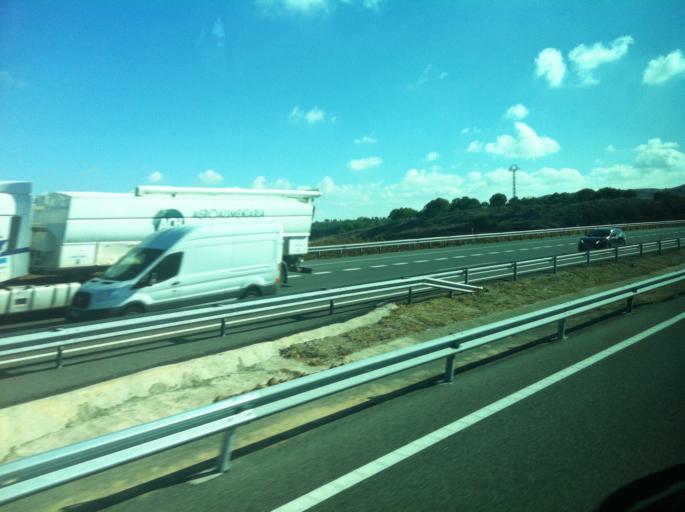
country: ES
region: Castille and Leon
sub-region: Provincia de Burgos
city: Fuentespina
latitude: 41.6215
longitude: -3.6894
